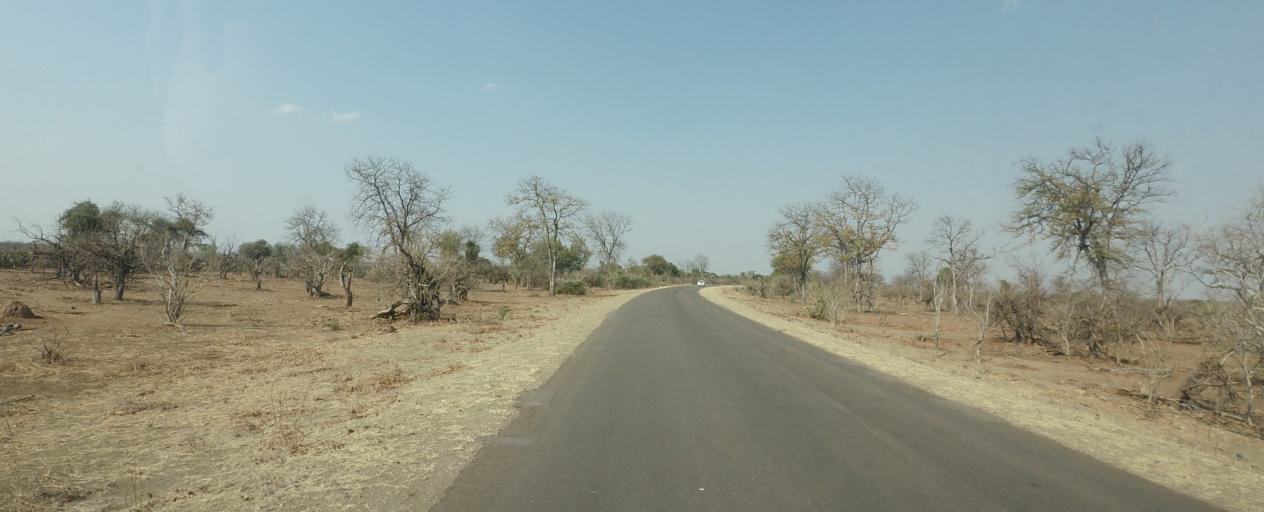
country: ZA
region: Limpopo
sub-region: Mopani District Municipality
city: Giyani
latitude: -23.0972
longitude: 31.3898
